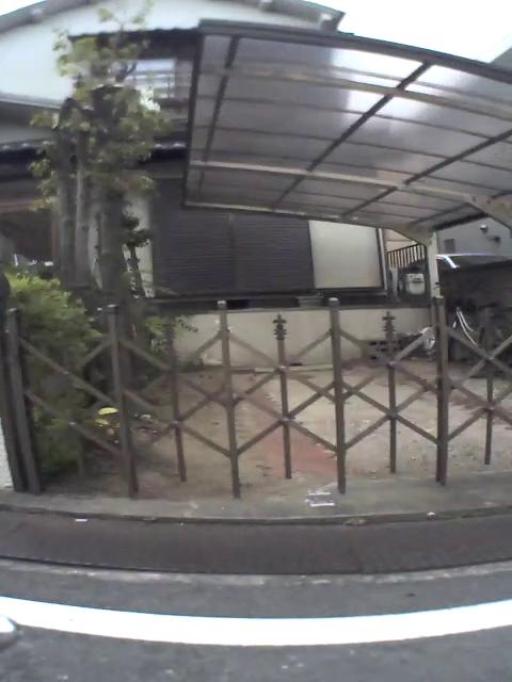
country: JP
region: Osaka
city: Neyagawa
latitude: 34.7842
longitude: 135.6410
